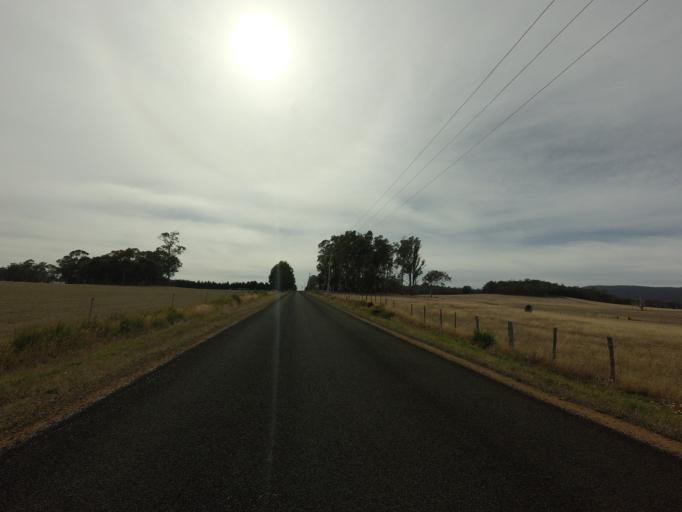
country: AU
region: Tasmania
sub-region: Sorell
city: Sorell
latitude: -42.4286
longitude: 147.4735
